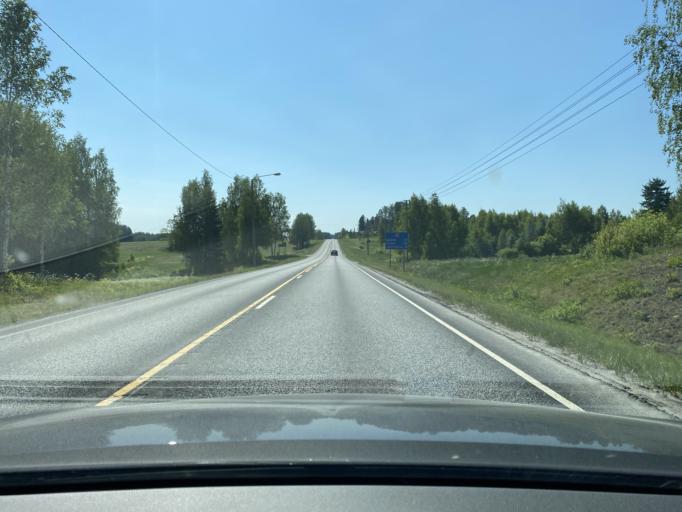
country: FI
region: Pirkanmaa
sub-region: Tampere
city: Nokia
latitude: 61.4228
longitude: 23.3374
